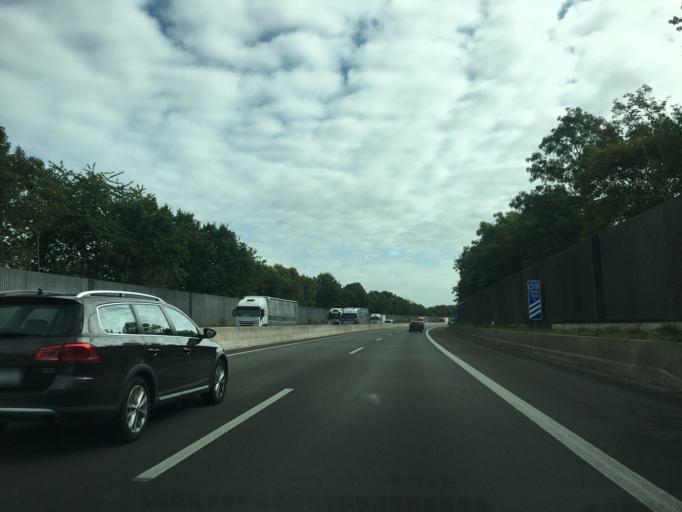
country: DE
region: North Rhine-Westphalia
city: Loehne
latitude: 52.2052
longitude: 8.7000
